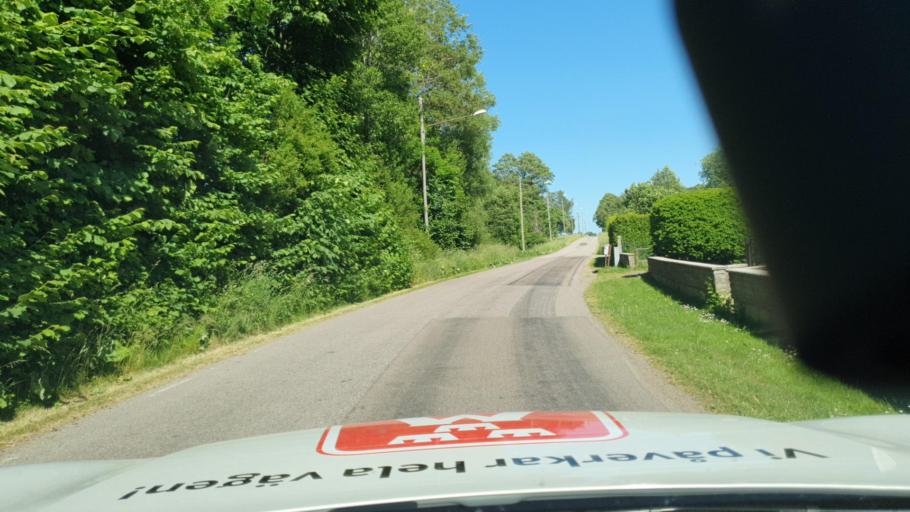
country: SE
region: Skane
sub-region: Sjobo Kommun
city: Sjoebo
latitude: 55.6376
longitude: 13.7775
